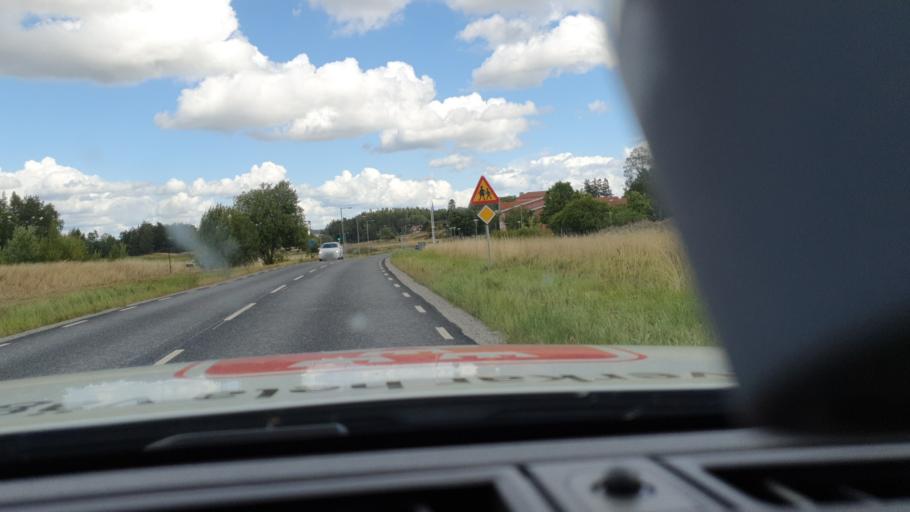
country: SE
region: Stockholm
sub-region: Osterakers Kommun
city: Akersberga
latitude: 59.4801
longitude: 18.2627
